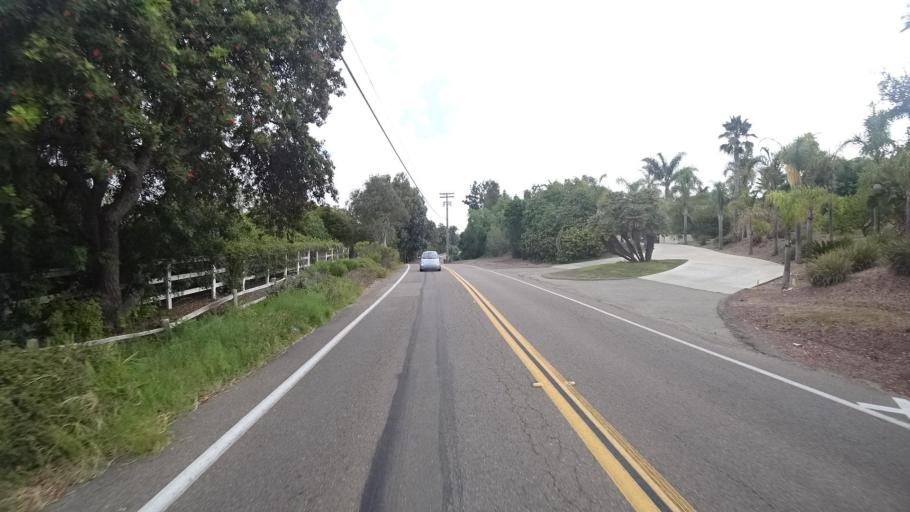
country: US
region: California
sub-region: San Diego County
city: Rancho Santa Fe
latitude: 33.0263
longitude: -117.2370
